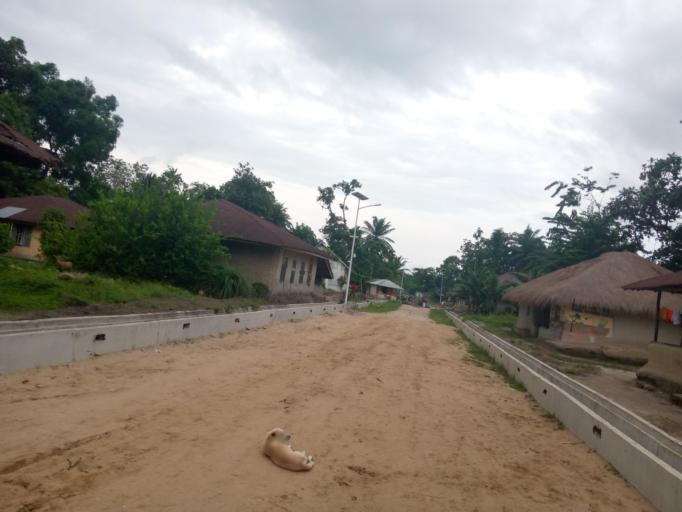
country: SL
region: Southern Province
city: Bonthe
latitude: 7.5269
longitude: -12.5069
